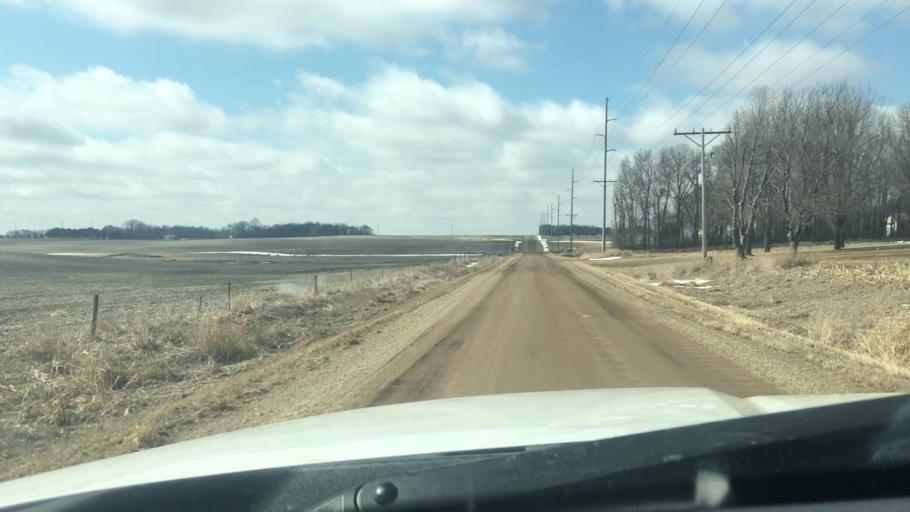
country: US
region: South Dakota
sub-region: Minnehaha County
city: Crooks
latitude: 43.6164
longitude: -96.7965
